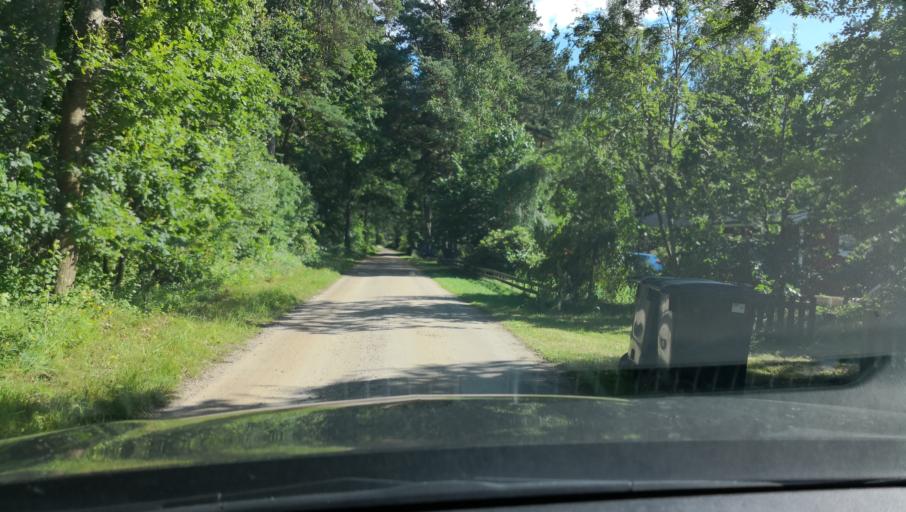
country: SE
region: Skane
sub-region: Kristianstads Kommun
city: Degeberga
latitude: 55.7943
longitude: 14.1953
